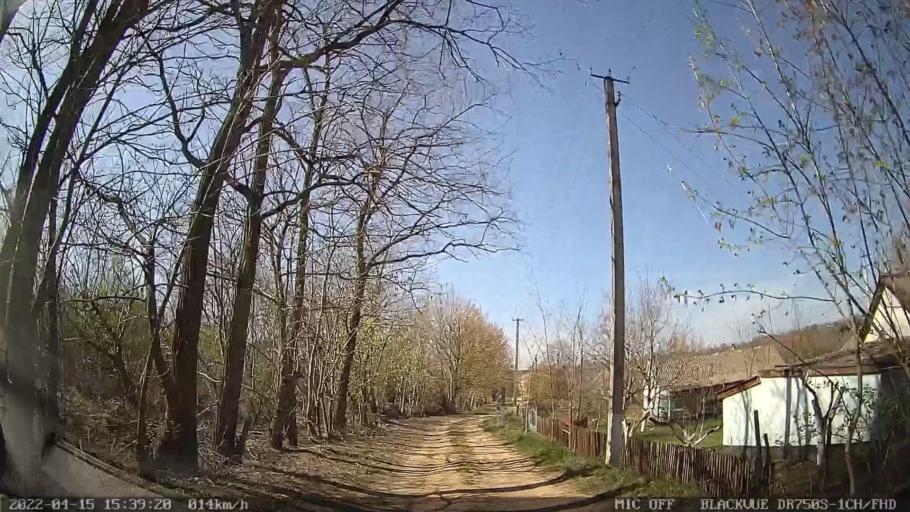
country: MD
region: Raionul Ocnita
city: Otaci
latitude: 48.3533
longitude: 27.9275
